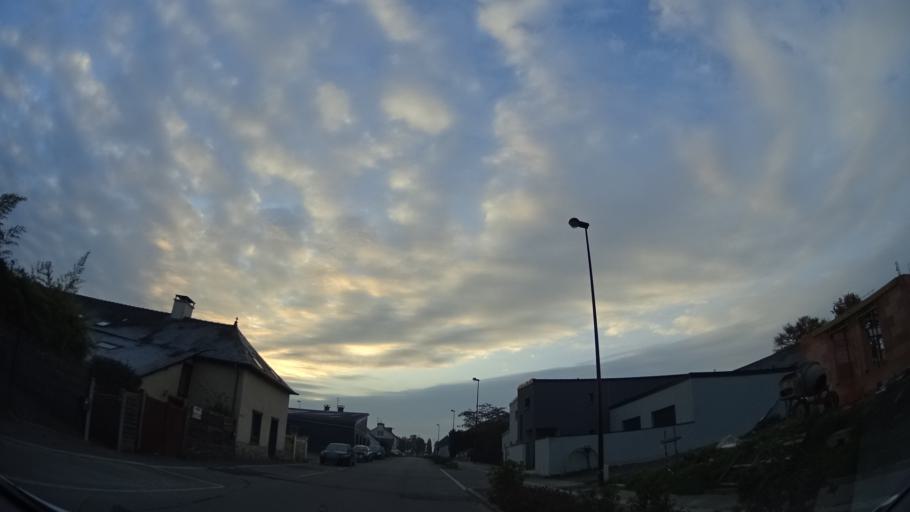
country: FR
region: Brittany
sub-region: Departement d'Ille-et-Vilaine
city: La Chapelle-des-Fougeretz
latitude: 48.2000
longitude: -1.7352
